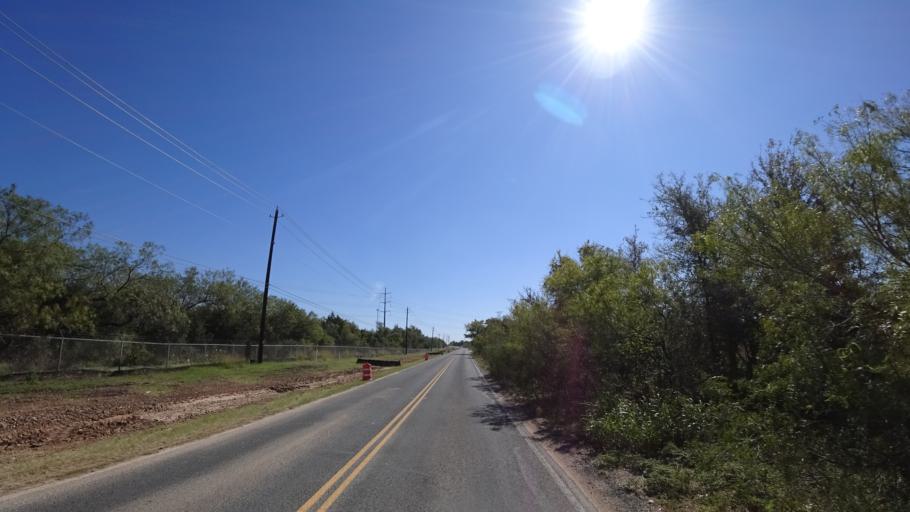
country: US
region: Texas
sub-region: Travis County
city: Hornsby Bend
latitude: 30.2785
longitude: -97.6064
